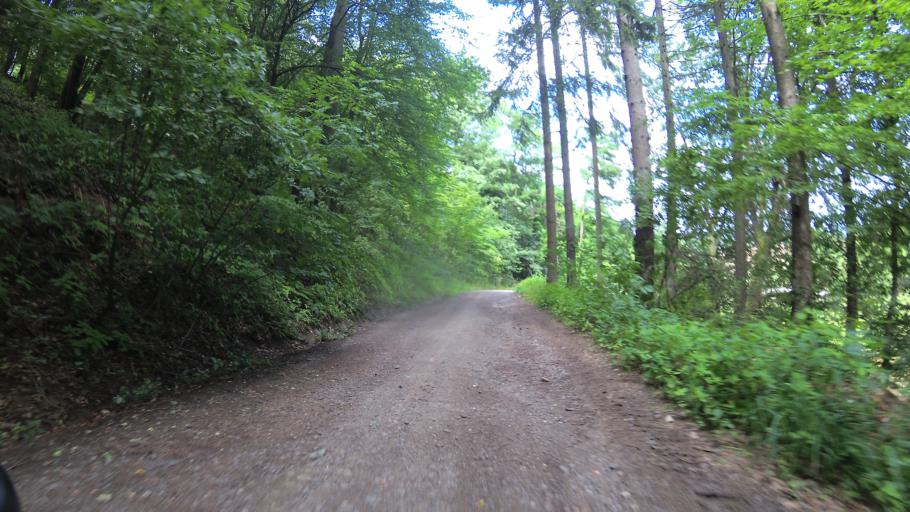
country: DE
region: Saarland
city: Marpingen
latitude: 49.4634
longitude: 7.1006
